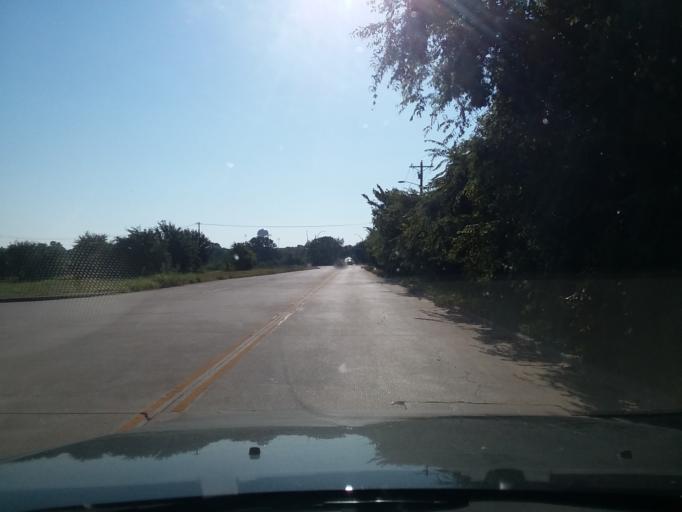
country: US
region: Texas
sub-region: Denton County
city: Double Oak
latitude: 33.0591
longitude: -97.0773
